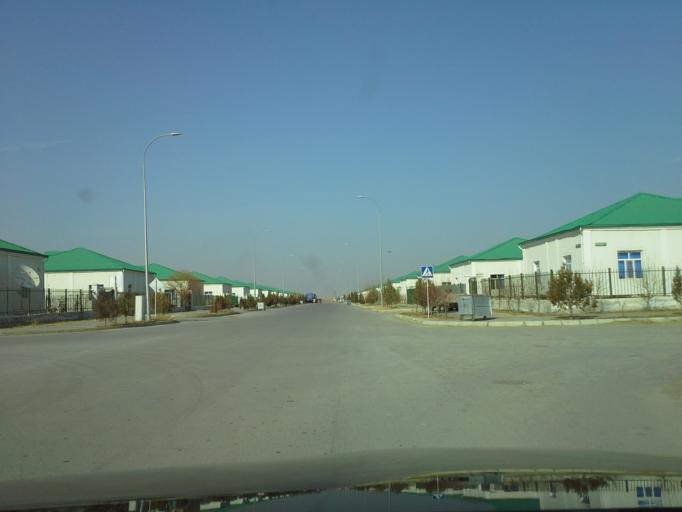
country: TM
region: Ahal
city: Abadan
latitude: 38.1671
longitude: 58.0521
